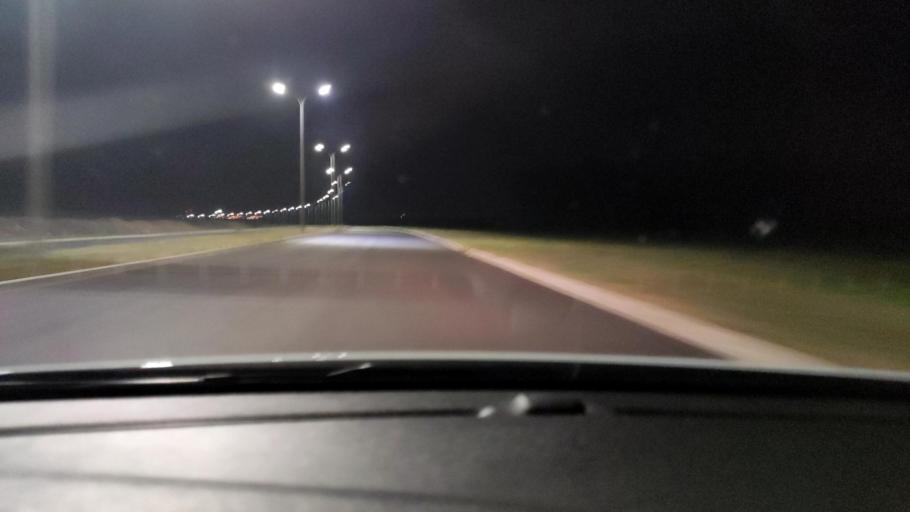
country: RU
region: Tatarstan
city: Sviyazhsk
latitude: 55.7395
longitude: 48.7421
